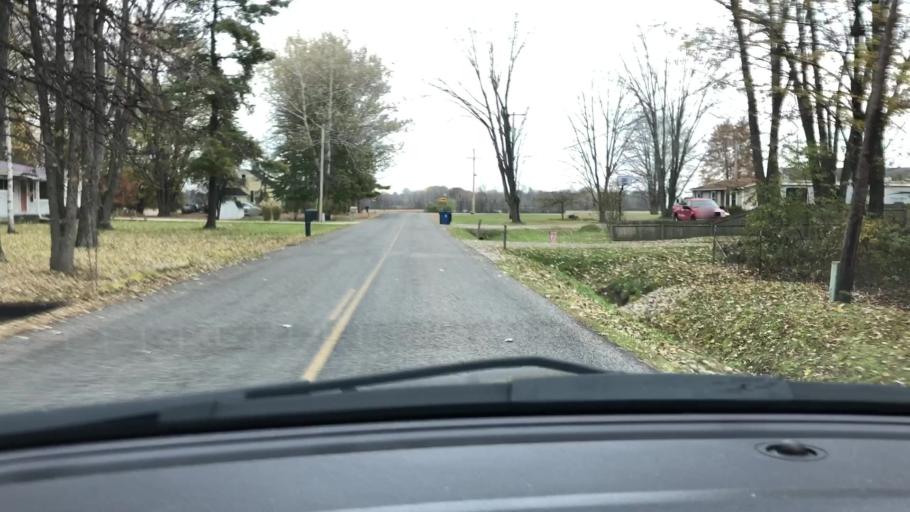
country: US
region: Michigan
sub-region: Midland County
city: Midland
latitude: 43.6412
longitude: -84.3321
